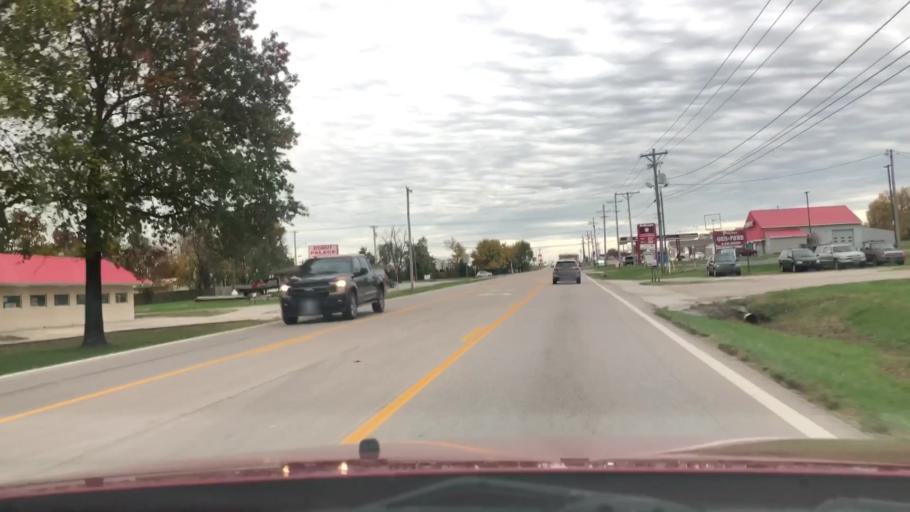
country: US
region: Missouri
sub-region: Dallas County
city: Buffalo
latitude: 37.6458
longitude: -93.1041
